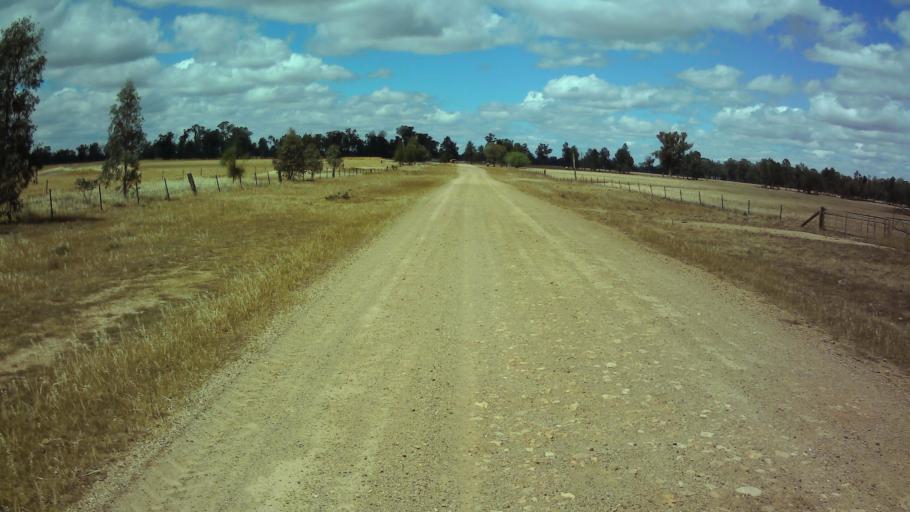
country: AU
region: New South Wales
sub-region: Weddin
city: Grenfell
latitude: -34.0120
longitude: 147.9161
